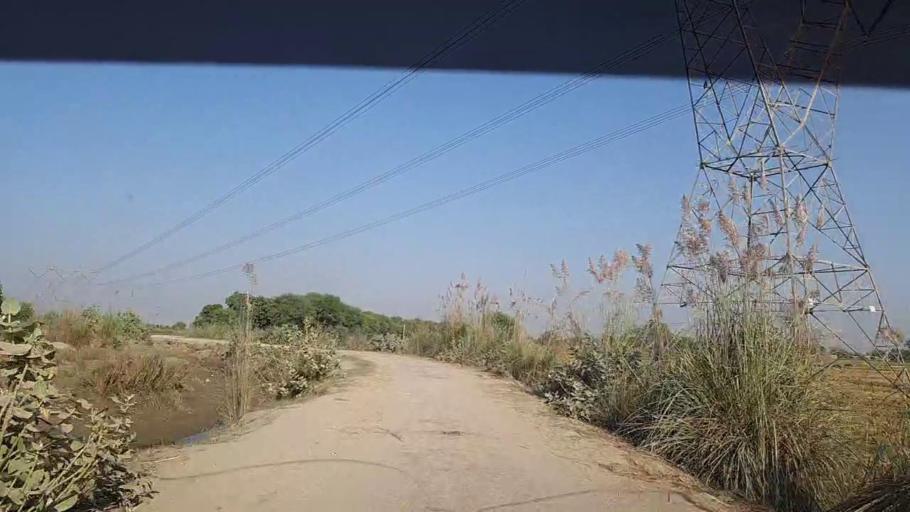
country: PK
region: Sindh
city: Larkana
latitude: 27.6253
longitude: 68.2533
